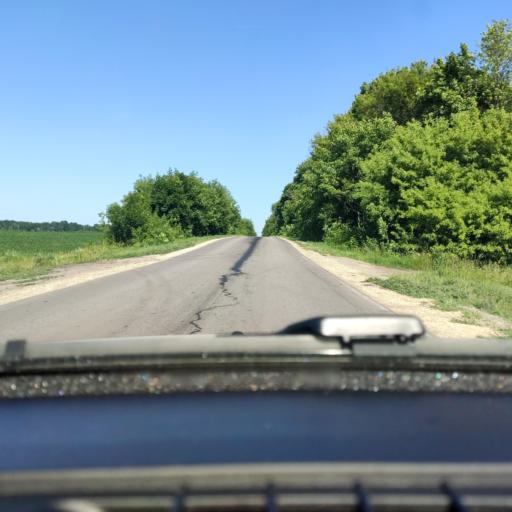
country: RU
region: Voronezj
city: Pereleshinskiy
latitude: 51.6182
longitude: 40.2386
